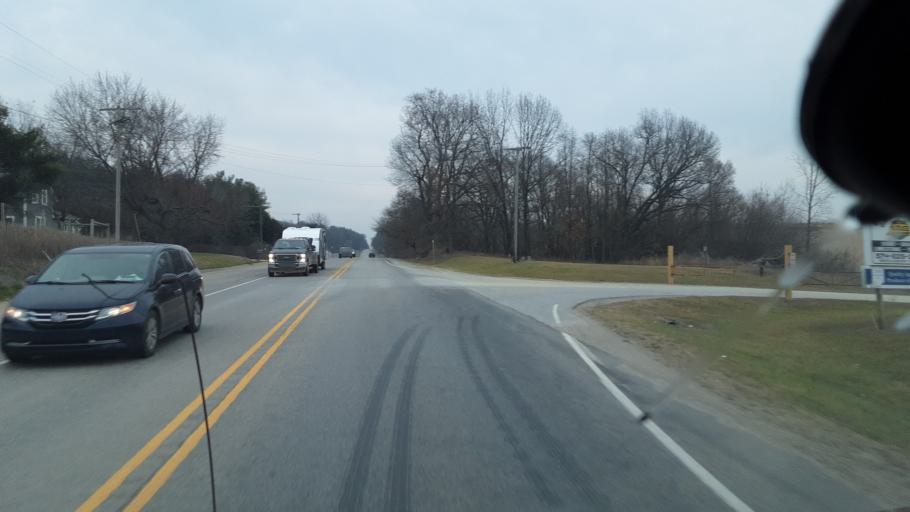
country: US
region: Indiana
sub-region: Elkhart County
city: Middlebury
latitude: 41.7259
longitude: -85.6562
